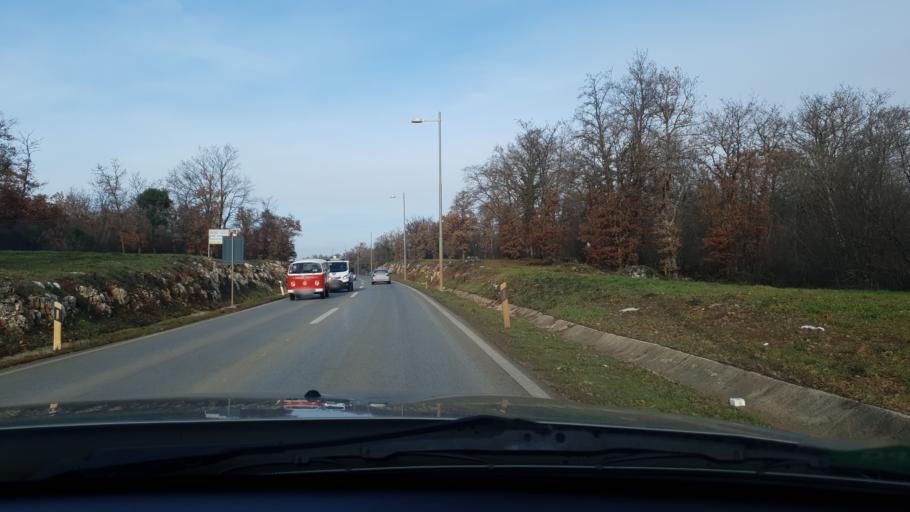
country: HR
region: Istarska
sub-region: Grad Porec
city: Porec
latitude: 45.2427
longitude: 13.6250
